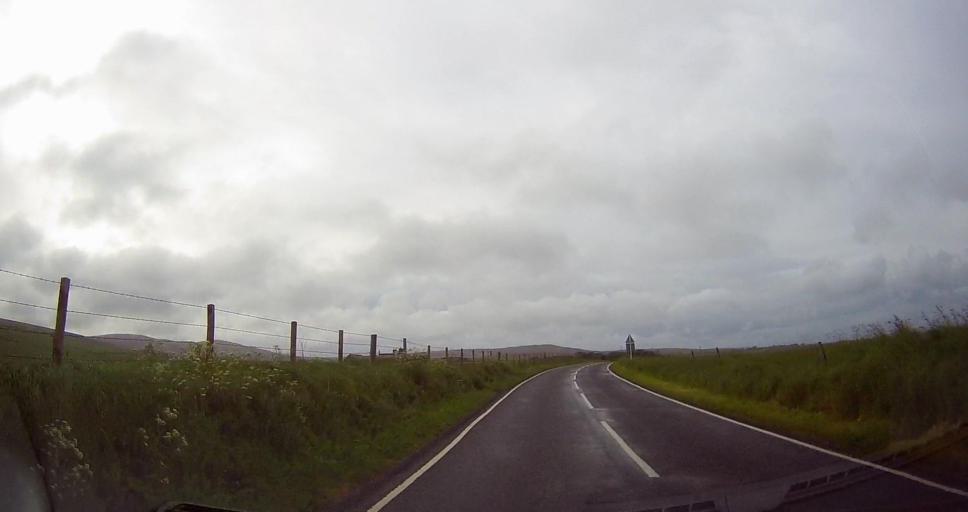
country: GB
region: Scotland
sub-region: Orkney Islands
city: Stromness
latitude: 58.9685
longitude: -3.2282
